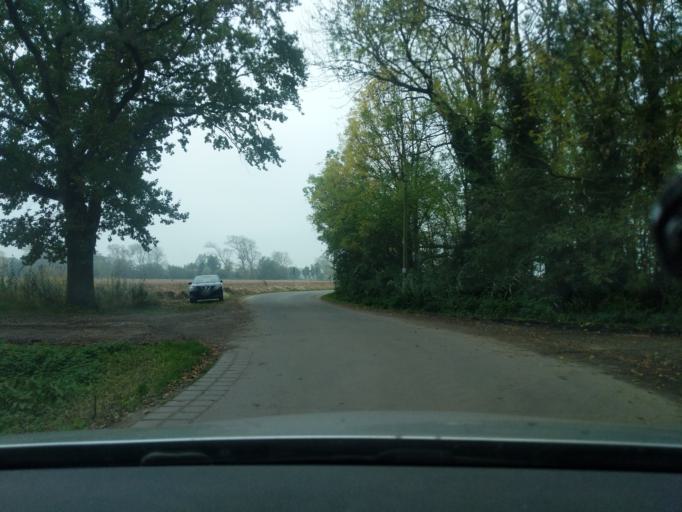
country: DE
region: Lower Saxony
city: Otterndorf
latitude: 53.8216
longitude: 8.8670
